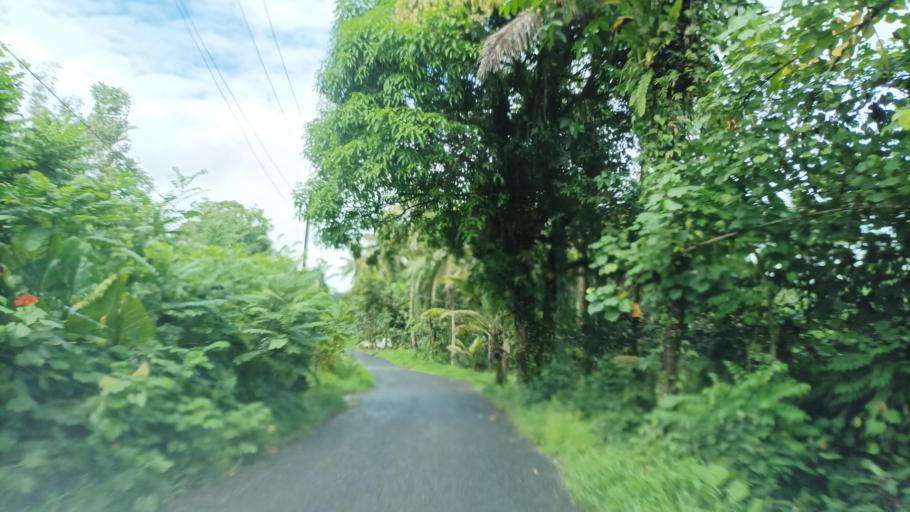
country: FM
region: Pohnpei
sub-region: Sokehs Municipality
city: Palikir - National Government Center
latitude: 6.9347
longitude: 158.1859
